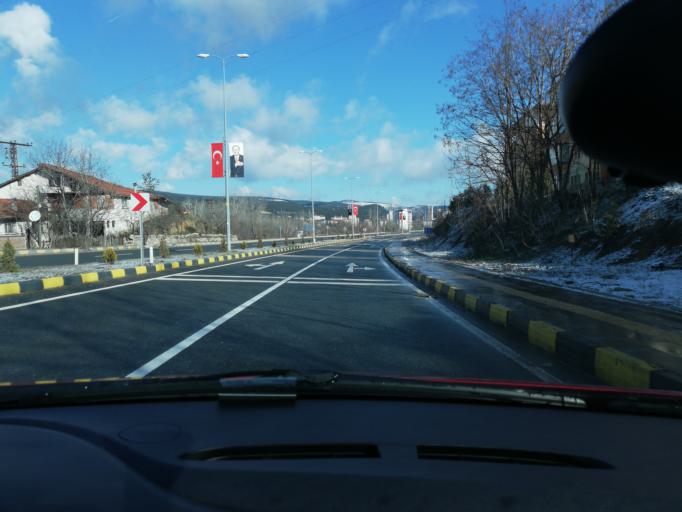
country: TR
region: Kastamonu
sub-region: Cide
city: Kastamonu
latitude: 41.3481
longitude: 33.7664
